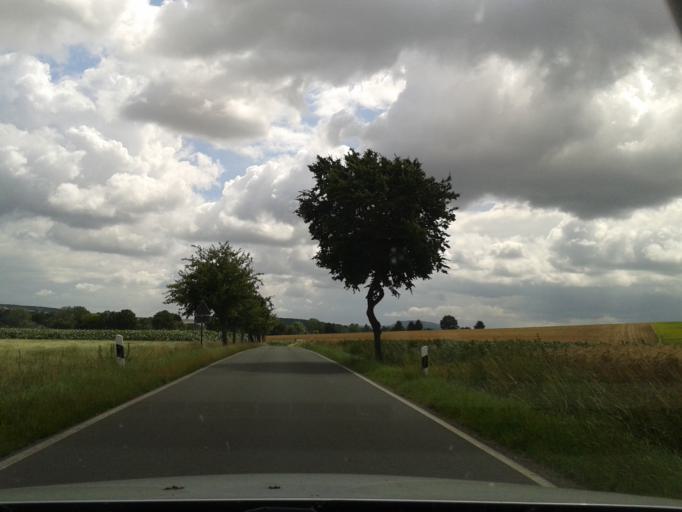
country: DE
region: North Rhine-Westphalia
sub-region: Regierungsbezirk Detmold
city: Dorentrup
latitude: 52.0154
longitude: 9.0496
